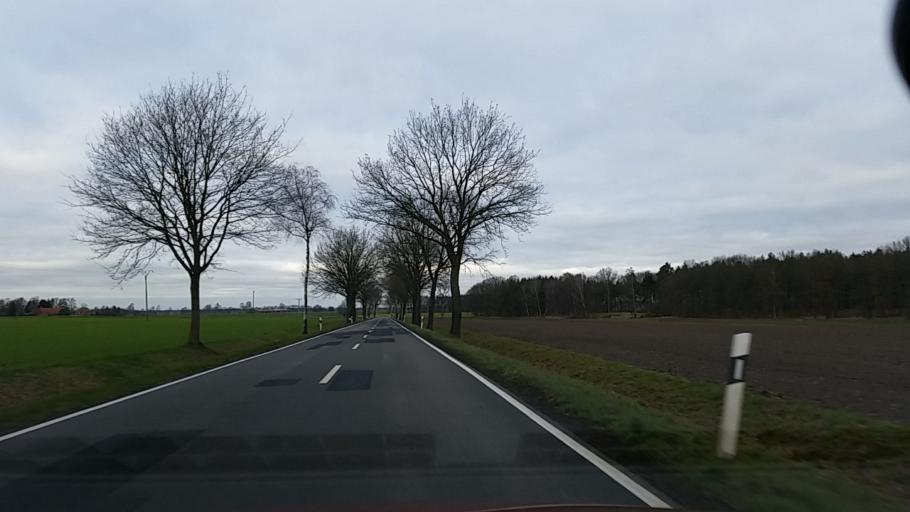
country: DE
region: Lower Saxony
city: Wittingen
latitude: 52.6904
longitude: 10.7531
